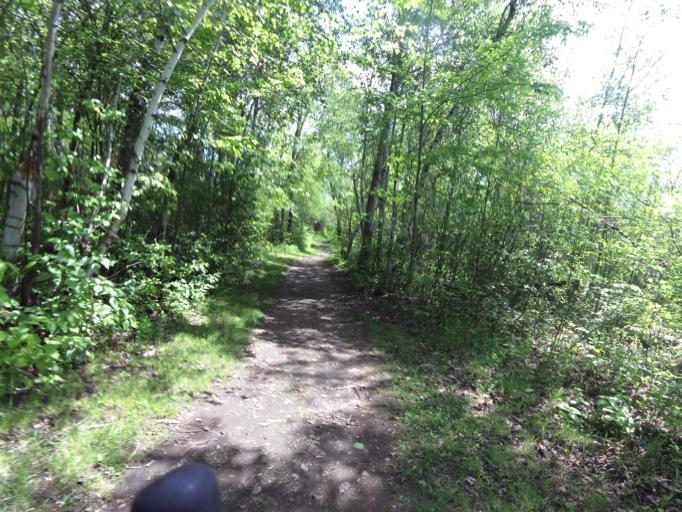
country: CA
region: Ontario
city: Ottawa
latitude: 45.3885
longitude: -75.5456
